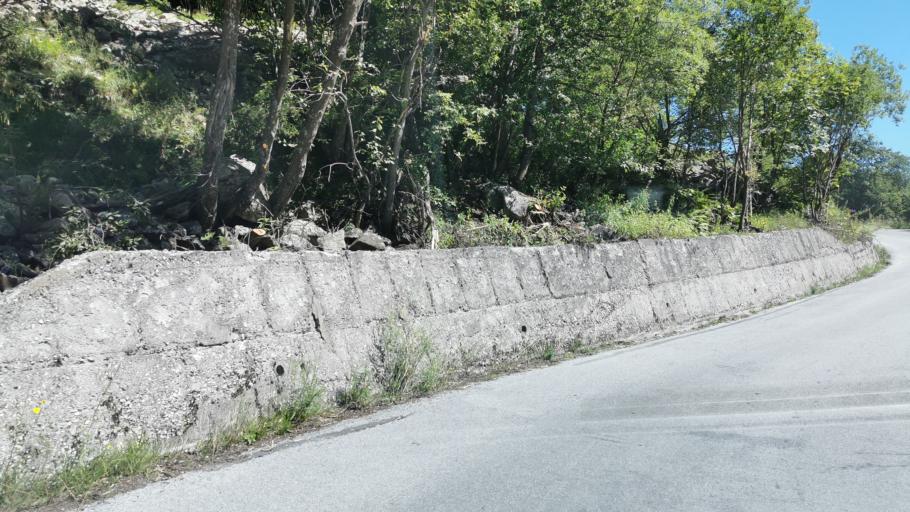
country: IT
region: Piedmont
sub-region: Provincia di Cuneo
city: Entracque
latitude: 44.1890
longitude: 7.3507
